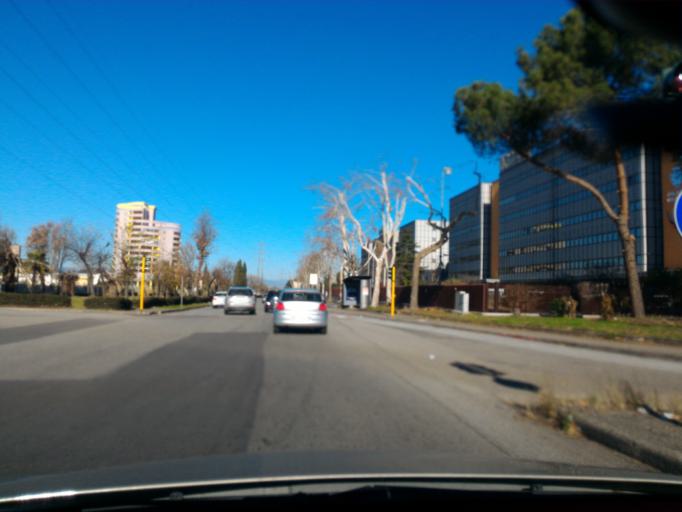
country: IT
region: Calabria
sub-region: Provincia di Cosenza
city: Cosenza
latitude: 39.3192
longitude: 16.2575
